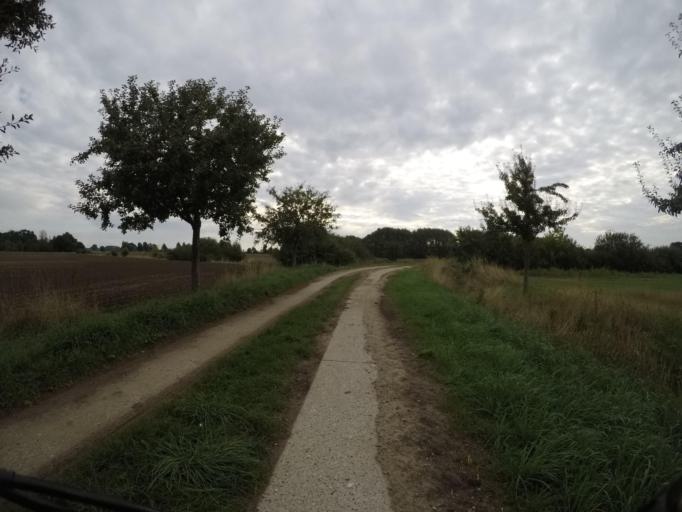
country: DE
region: Lower Saxony
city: Neu Darchau
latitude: 53.2906
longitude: 10.8652
